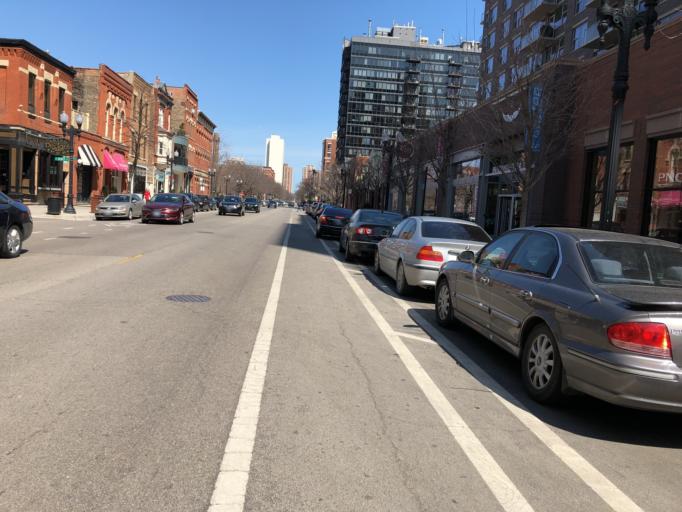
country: US
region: Illinois
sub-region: Cook County
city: Chicago
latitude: 41.9047
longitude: -87.6344
